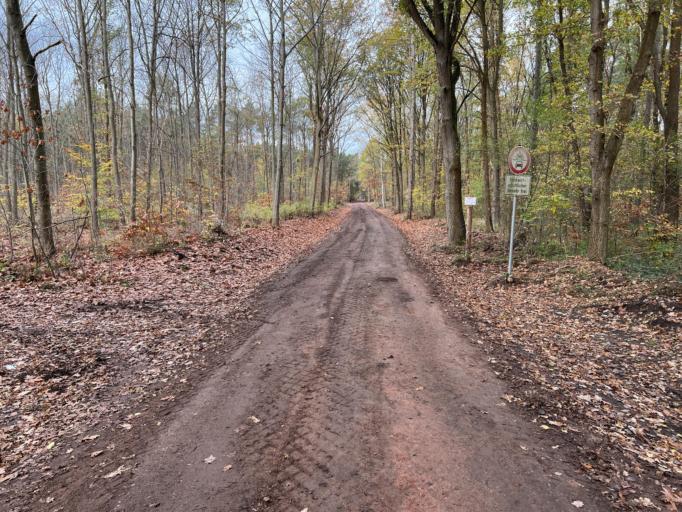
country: DE
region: Saxony-Anhalt
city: Raguhn
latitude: 51.7524
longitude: 12.2173
